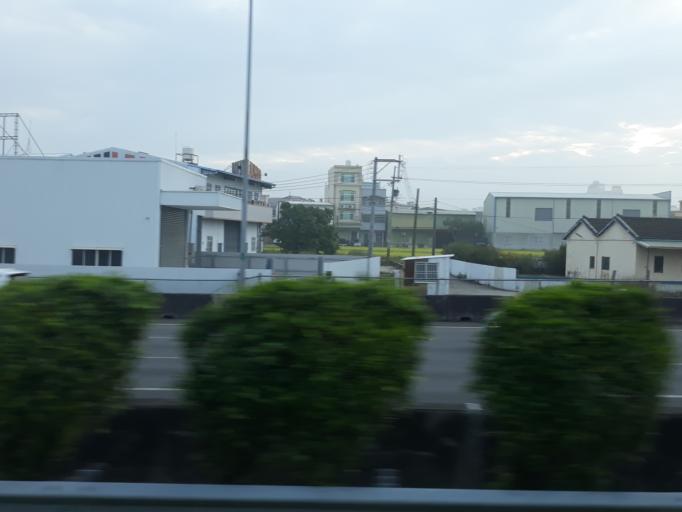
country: TW
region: Taiwan
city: Fengyuan
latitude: 24.2558
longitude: 120.6910
